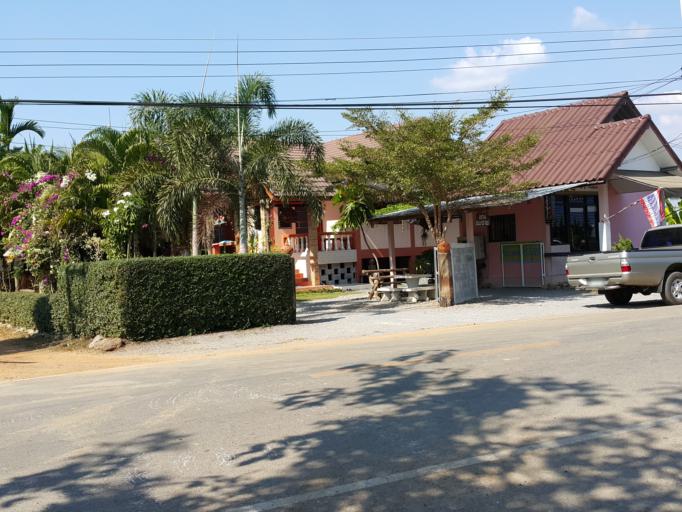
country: TH
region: Sukhothai
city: Thung Saliam
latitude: 17.3223
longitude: 99.5494
